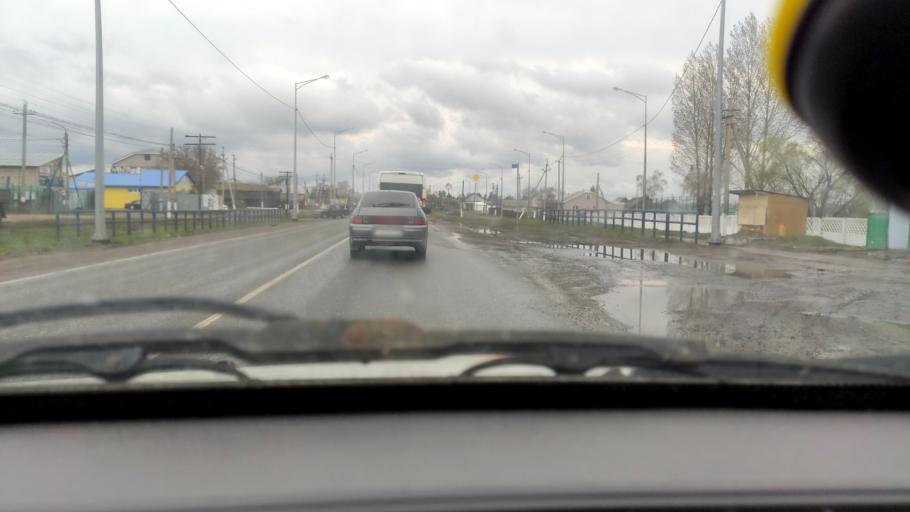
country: RU
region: Samara
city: Zhigulevsk
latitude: 53.5502
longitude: 49.5249
